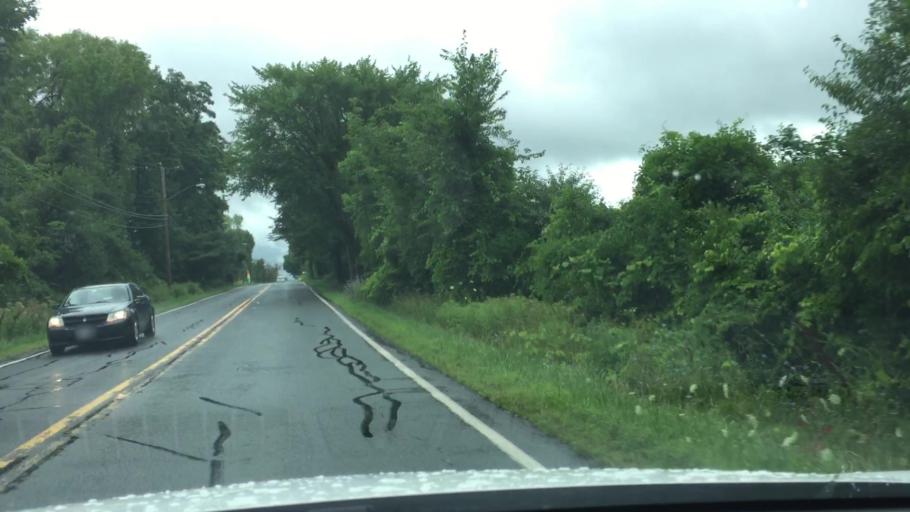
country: US
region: Massachusetts
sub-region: Berkshire County
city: Lenox
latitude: 42.4188
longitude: -73.3094
